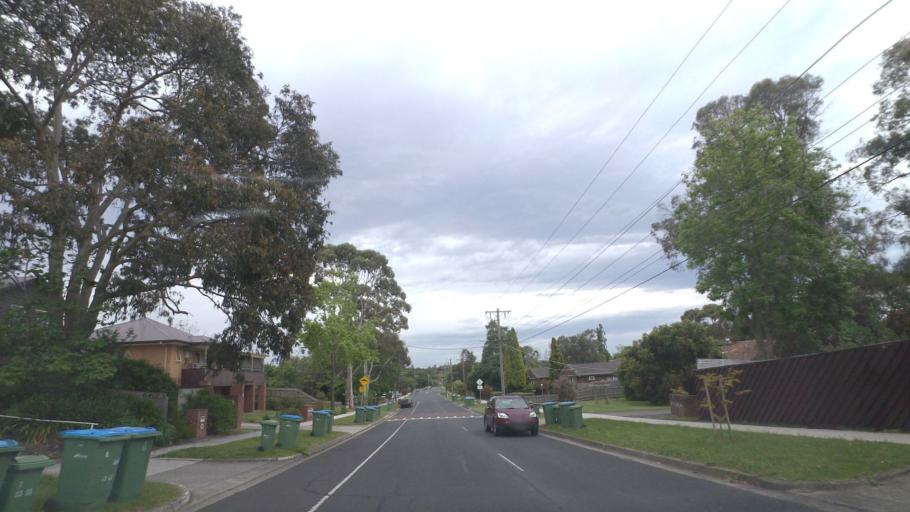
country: AU
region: Victoria
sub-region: Maroondah
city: Croydon South
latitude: -37.7976
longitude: 145.2586
